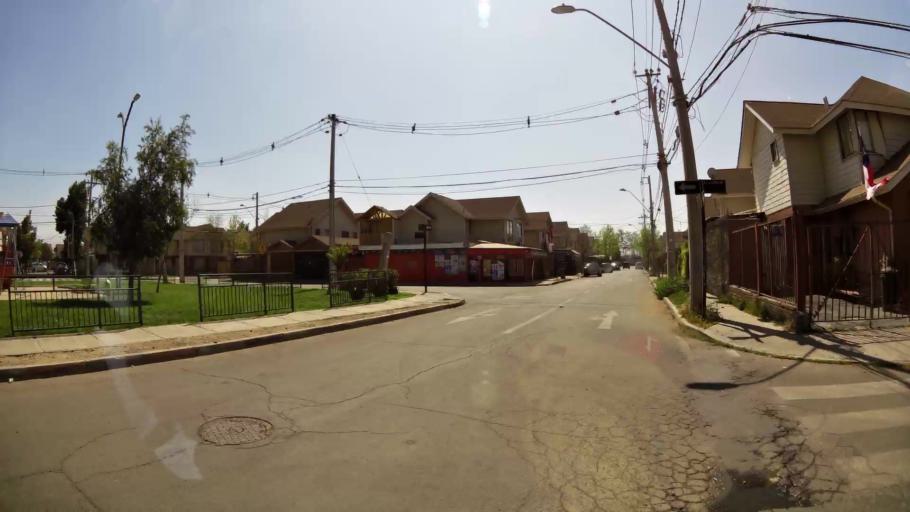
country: CL
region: Santiago Metropolitan
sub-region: Provincia de Santiago
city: Lo Prado
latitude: -33.3513
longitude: -70.7221
